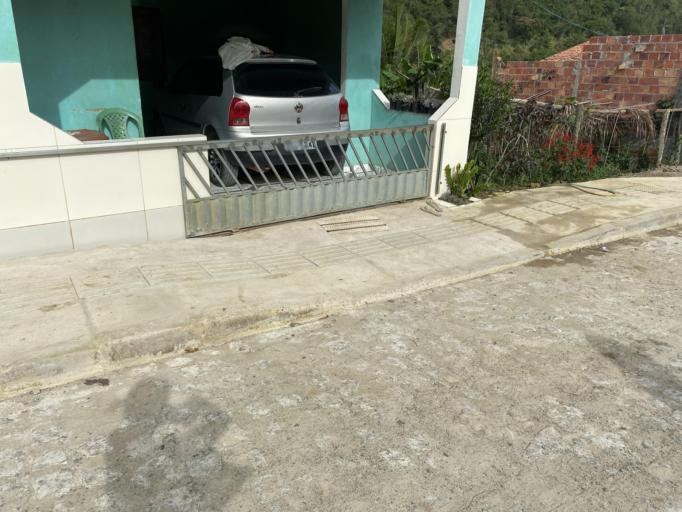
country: BR
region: Bahia
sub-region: Mutuipe
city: Mutuipe
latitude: -13.2556
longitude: -39.5651
